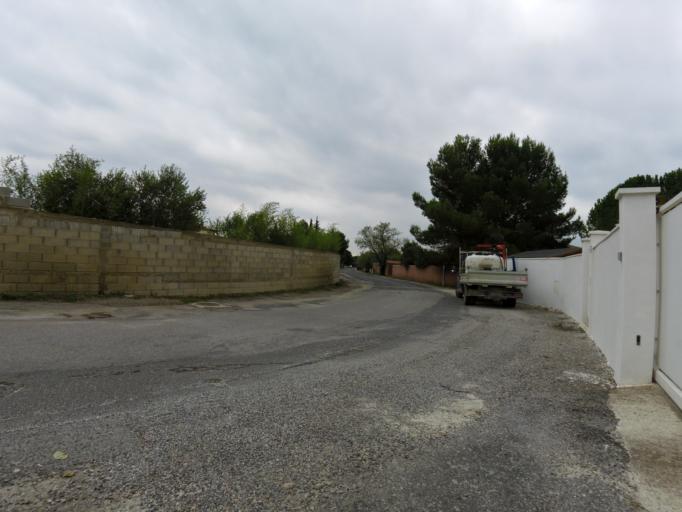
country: FR
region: Languedoc-Roussillon
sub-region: Departement de l'Herault
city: Villetelle
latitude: 43.7228
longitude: 4.1339
